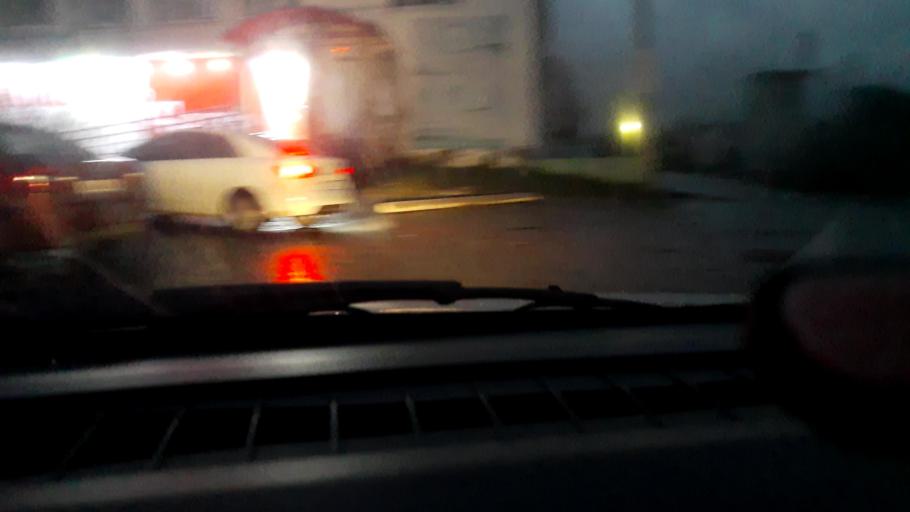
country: RU
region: Nizjnij Novgorod
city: Uren'
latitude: 57.4547
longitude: 45.7888
